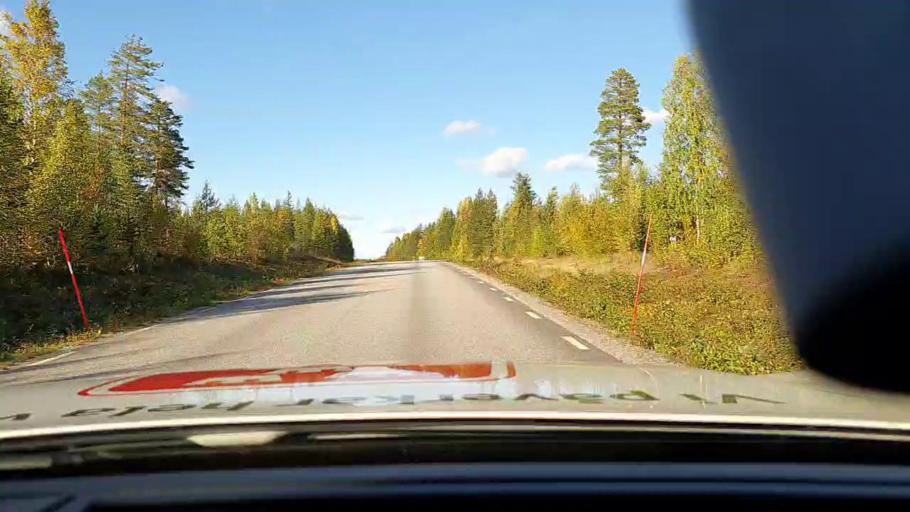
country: SE
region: Norrbotten
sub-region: Pitea Kommun
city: Norrfjarden
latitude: 65.4950
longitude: 21.4745
